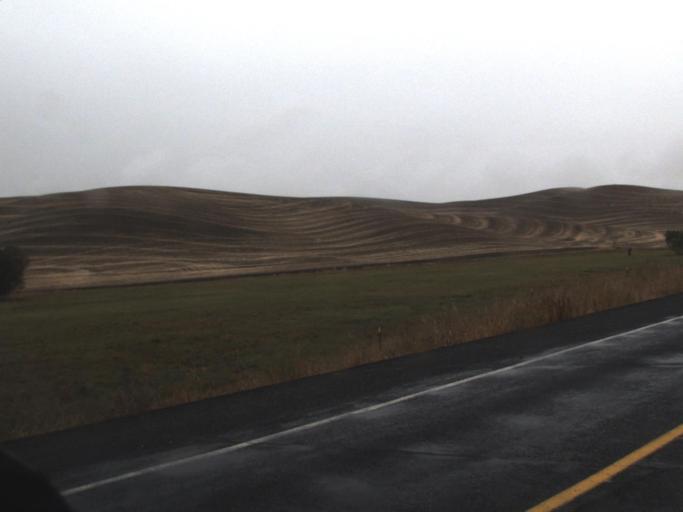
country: US
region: Washington
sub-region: Whitman County
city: Colfax
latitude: 47.0042
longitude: -117.3606
